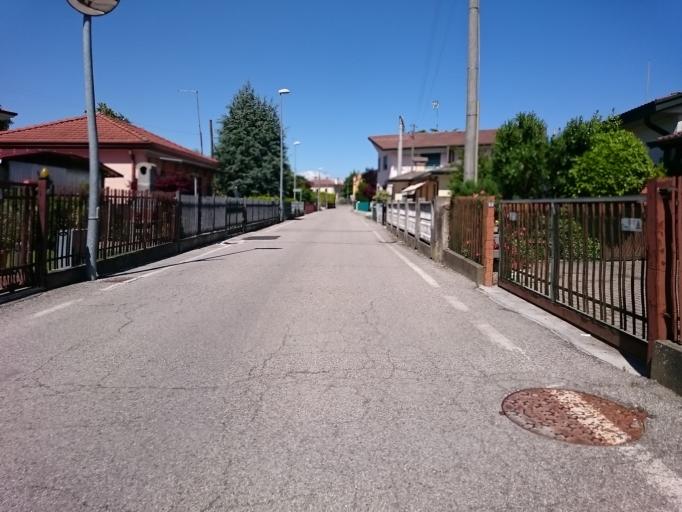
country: IT
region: Veneto
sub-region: Provincia di Padova
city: Codevigo
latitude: 45.2649
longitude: 12.1020
